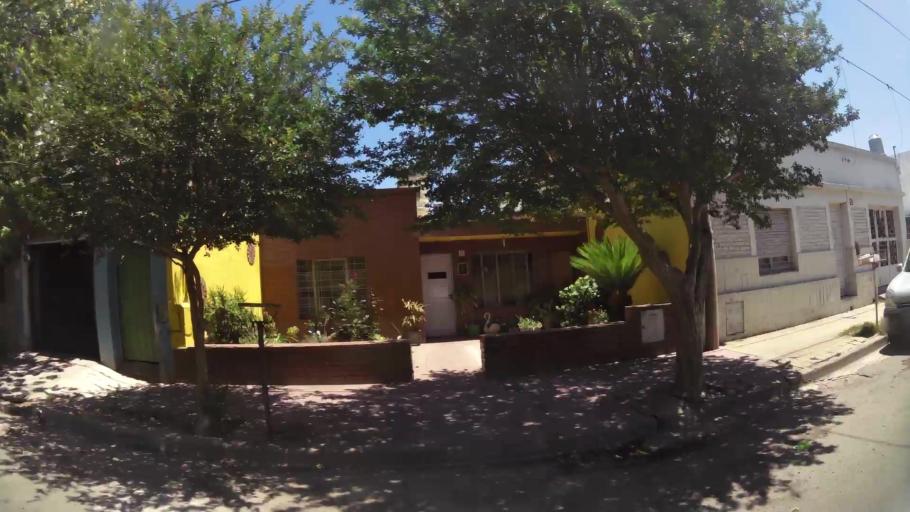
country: AR
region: Cordoba
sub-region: Departamento de Capital
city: Cordoba
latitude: -31.3829
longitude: -64.1357
